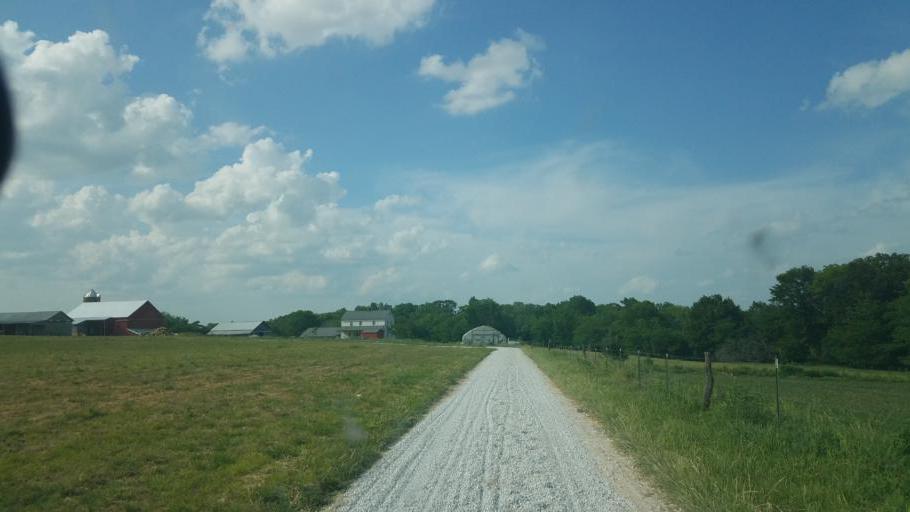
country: US
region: Missouri
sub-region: Cooper County
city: Boonville
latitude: 38.8547
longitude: -92.6463
